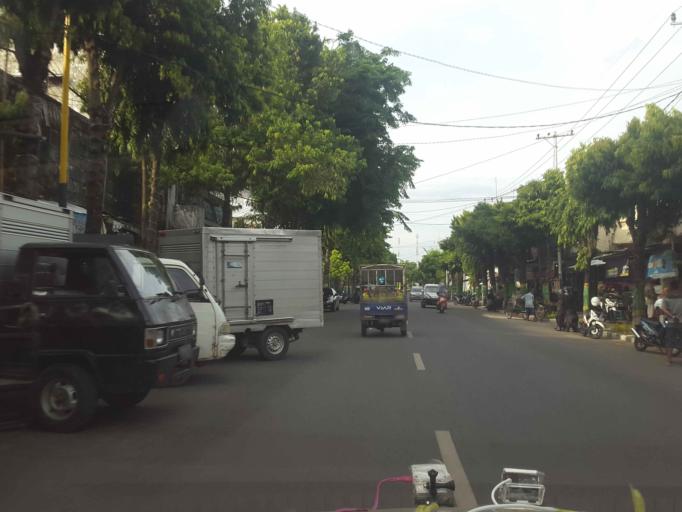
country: ID
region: East Java
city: Sumenep
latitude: -7.0050
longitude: 113.8603
